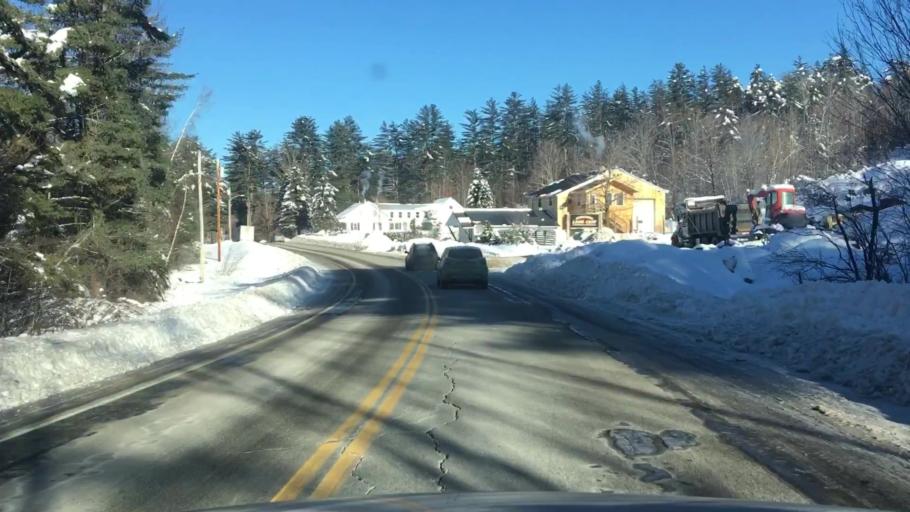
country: US
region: Maine
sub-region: Oxford County
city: West Paris
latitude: 44.4050
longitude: -70.6350
